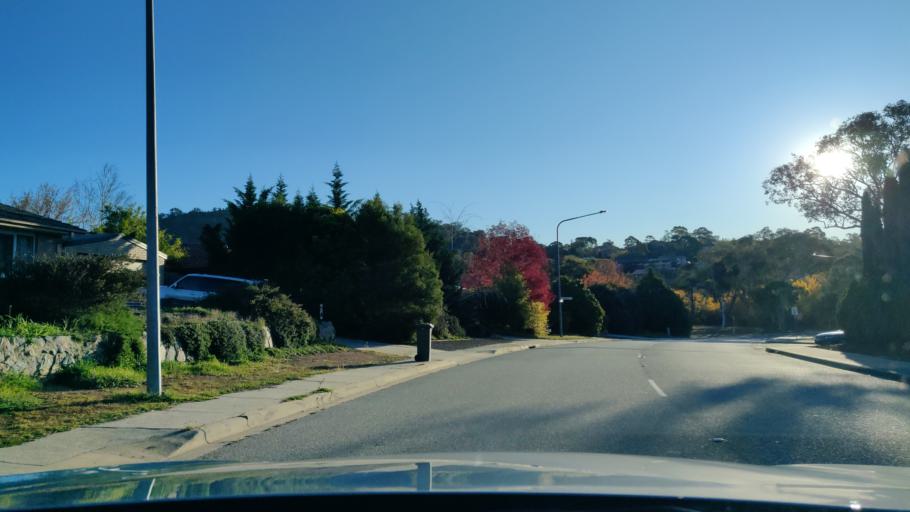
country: AU
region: Australian Capital Territory
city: Macarthur
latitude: -35.4499
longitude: 149.1225
